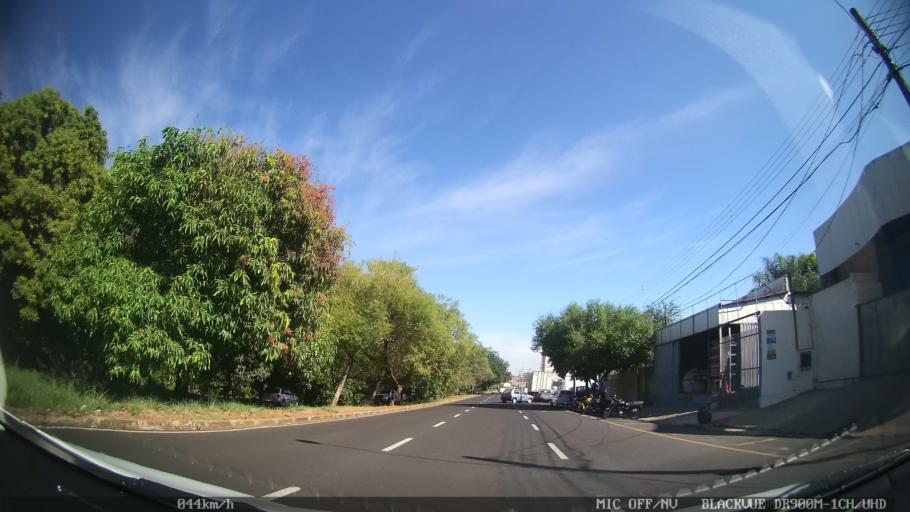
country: BR
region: Sao Paulo
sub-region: Sao Jose Do Rio Preto
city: Sao Jose do Rio Preto
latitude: -20.7859
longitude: -49.3720
